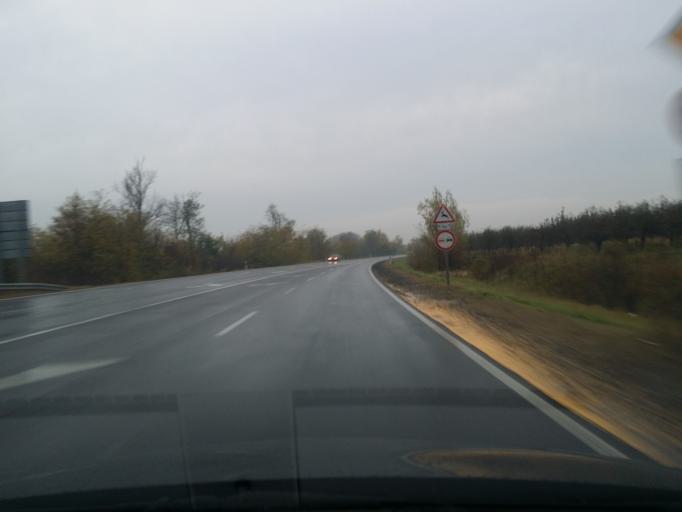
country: HU
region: Szabolcs-Szatmar-Bereg
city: Nyirbogdany
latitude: 48.0207
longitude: 21.8432
